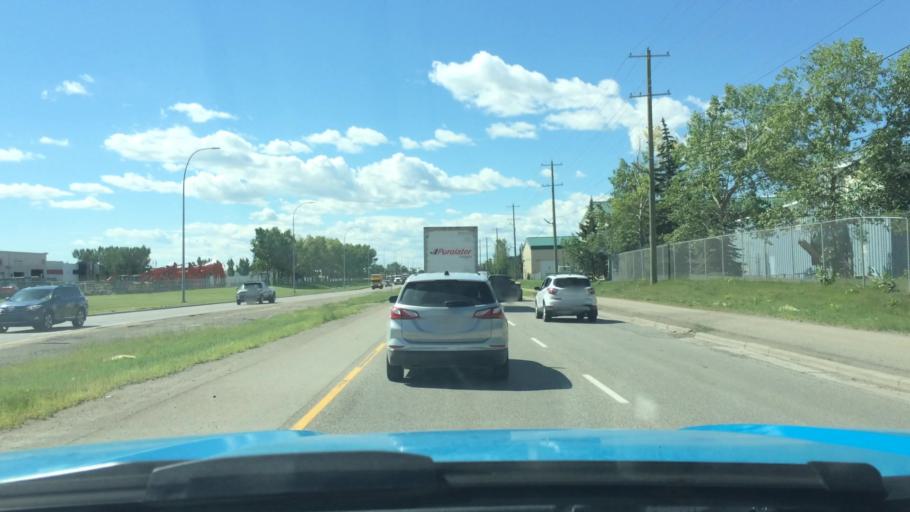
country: CA
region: Alberta
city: Calgary
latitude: 51.0030
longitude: -113.9587
